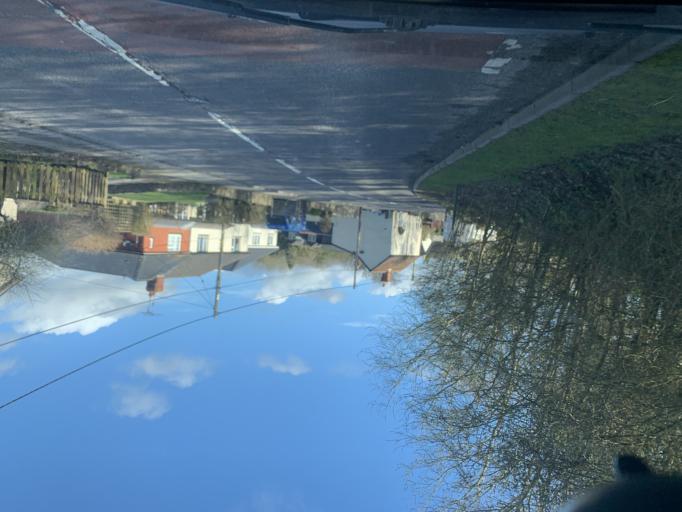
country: GB
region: England
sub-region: Wiltshire
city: Stockton
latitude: 51.1936
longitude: -2.0099
